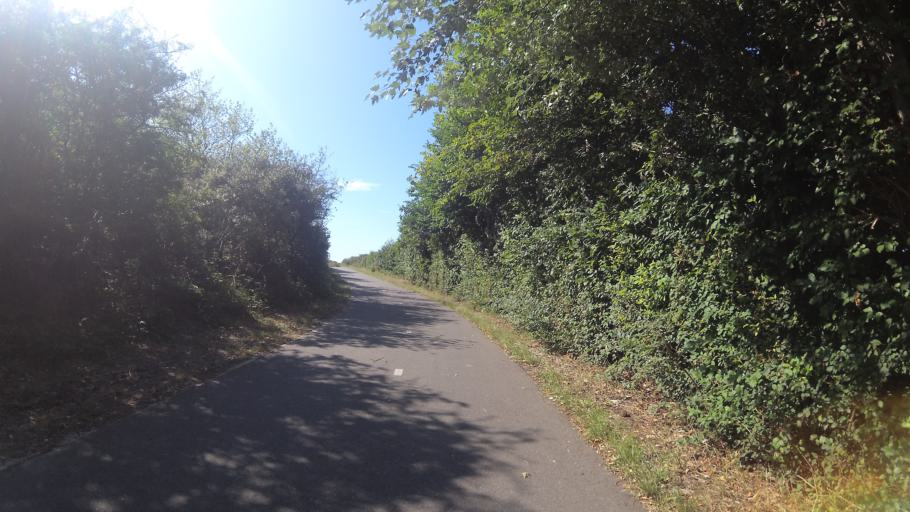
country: NL
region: Zeeland
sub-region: Gemeente Vlissingen
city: Vlissingen
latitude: 51.5150
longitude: 3.4537
